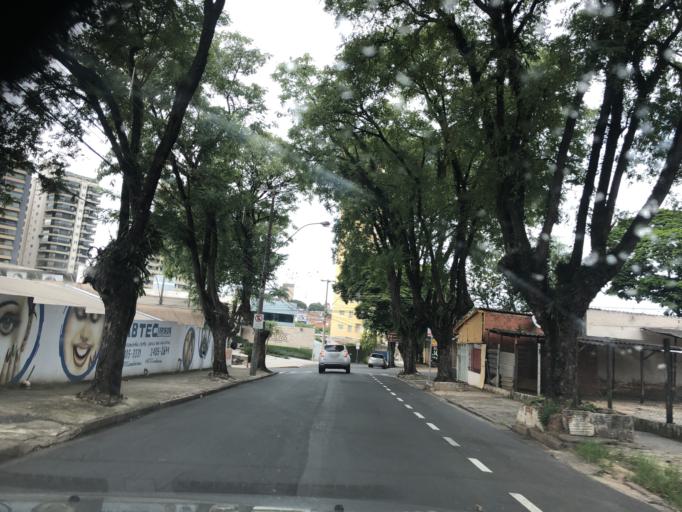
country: BR
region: Sao Paulo
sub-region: Americana
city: Americana
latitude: -22.7412
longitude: -47.3317
